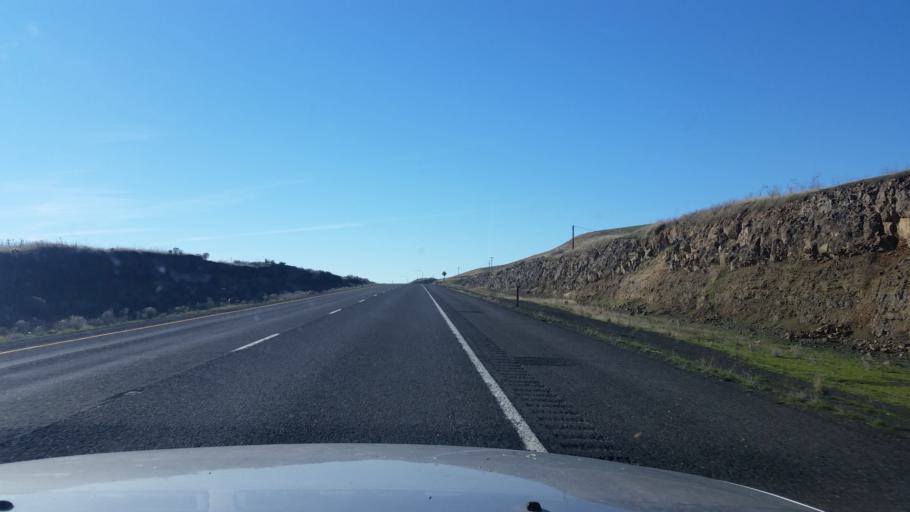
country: US
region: Washington
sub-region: Lincoln County
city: Davenport
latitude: 47.2944
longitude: -118.0314
